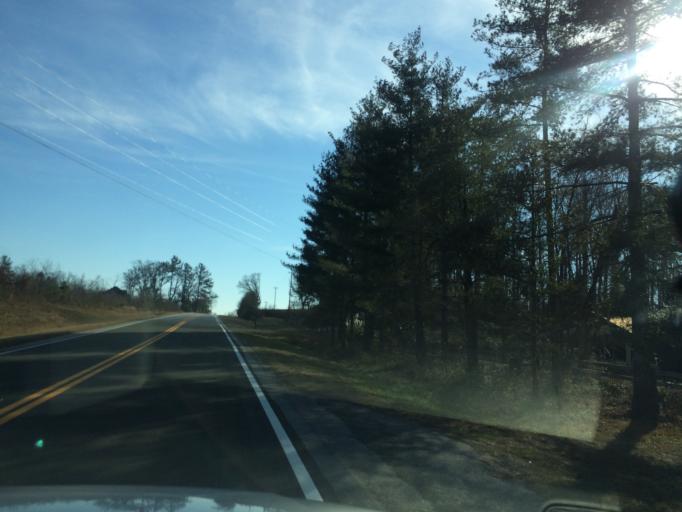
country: US
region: Georgia
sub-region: Franklin County
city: Lavonia
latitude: 34.4264
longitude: -83.0273
